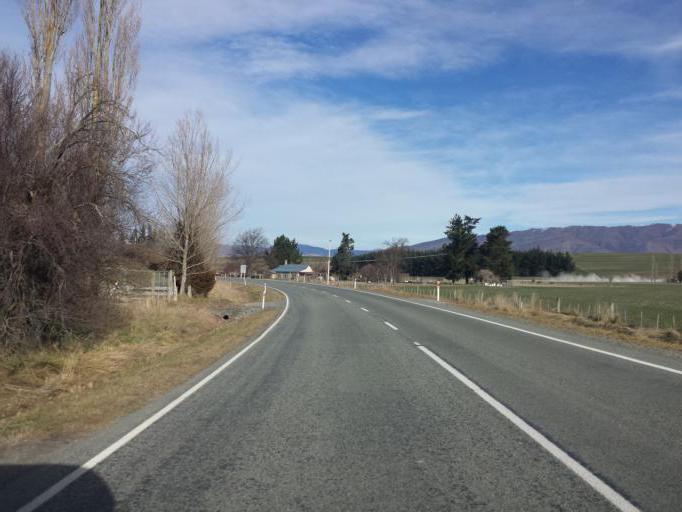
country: NZ
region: Canterbury
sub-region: Timaru District
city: Pleasant Point
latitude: -44.0681
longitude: 170.8684
